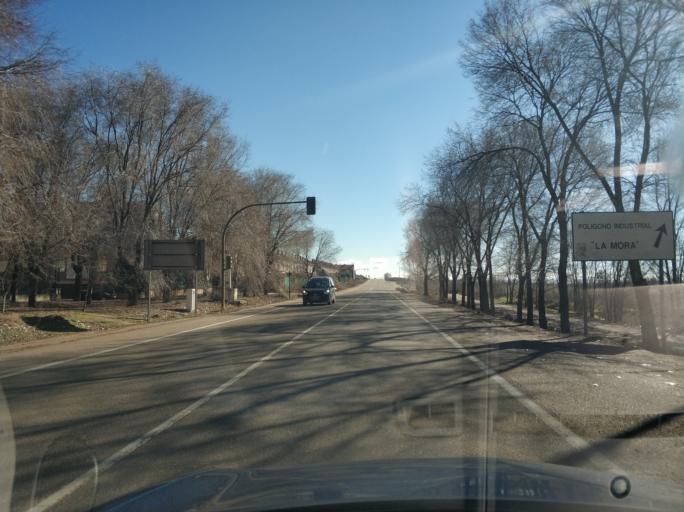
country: ES
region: Castille and Leon
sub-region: Provincia de Valladolid
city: Cisterniga
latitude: 41.6079
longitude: -4.6830
